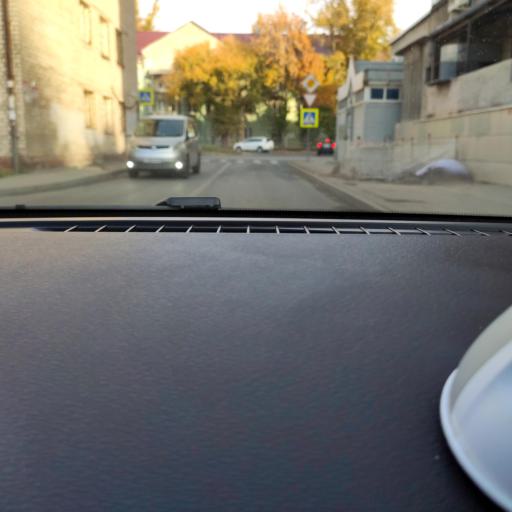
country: RU
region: Samara
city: Samara
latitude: 53.1935
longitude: 50.1315
